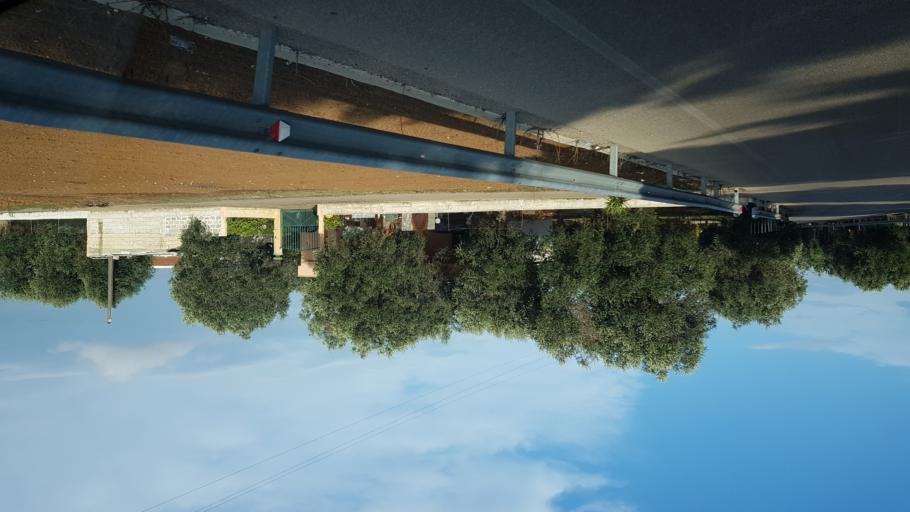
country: IT
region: Apulia
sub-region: Provincia di Brindisi
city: Oria
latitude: 40.5261
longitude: 17.6539
